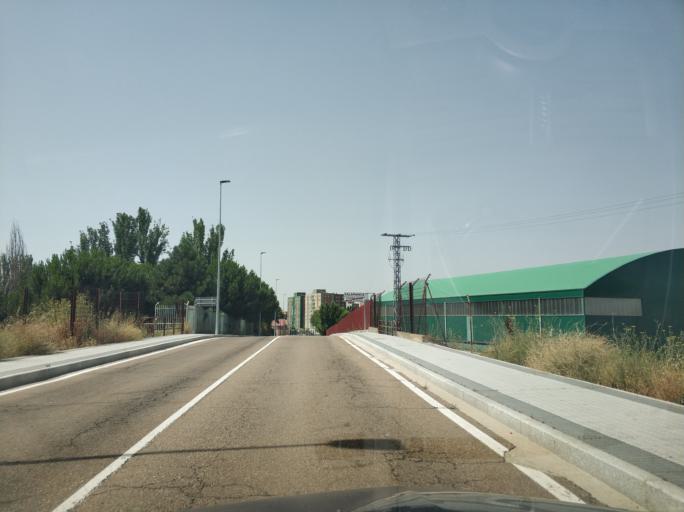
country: ES
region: Castille and Leon
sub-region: Provincia de Salamanca
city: Carbajosa de la Sagrada
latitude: 40.9454
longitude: -5.6597
